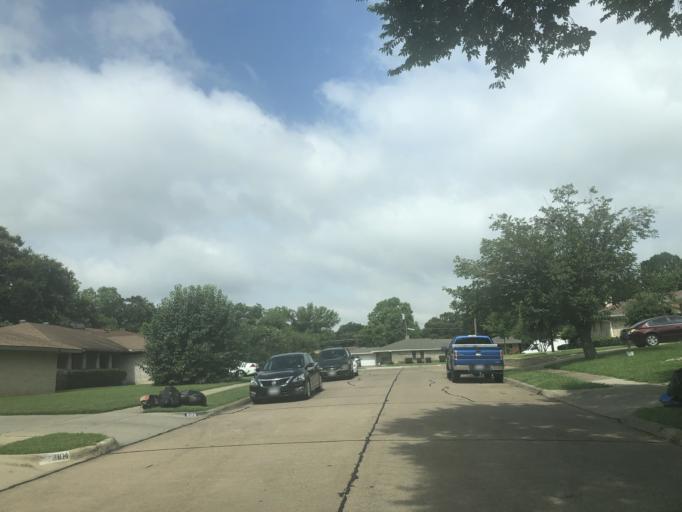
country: US
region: Texas
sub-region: Dallas County
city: Irving
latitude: 32.8000
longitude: -96.9721
